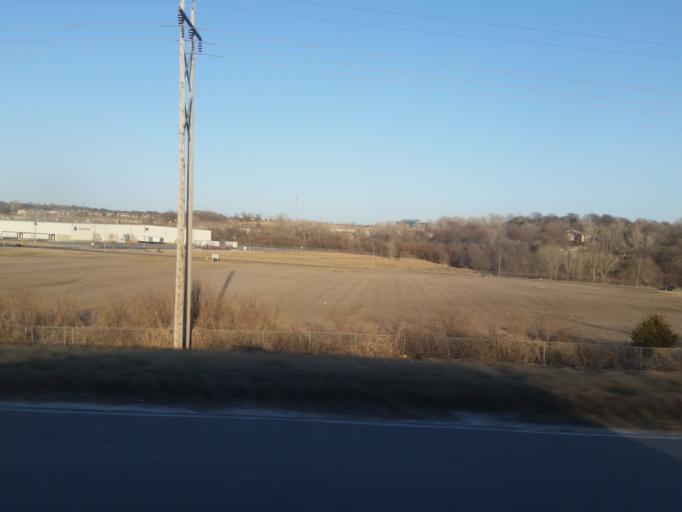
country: US
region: Nebraska
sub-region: Sarpy County
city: Offutt Air Force Base
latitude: 41.1529
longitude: -95.9386
